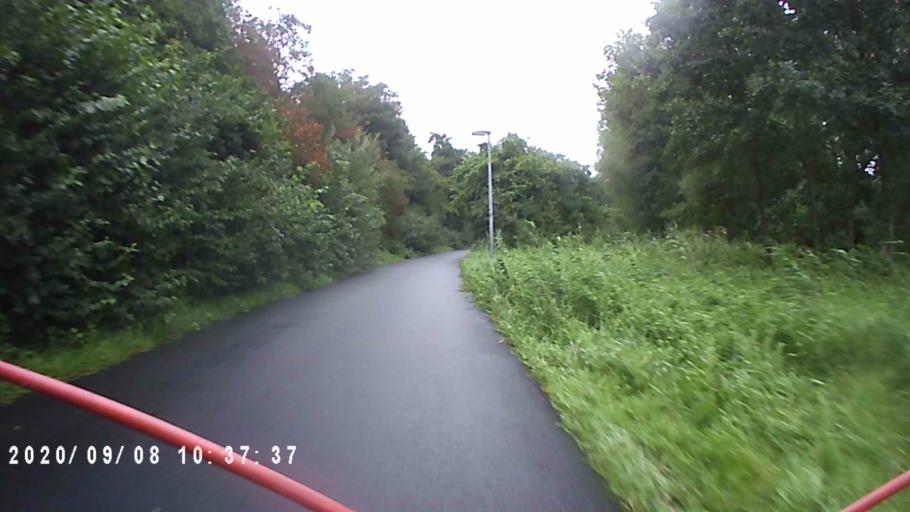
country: NL
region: Groningen
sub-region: Gemeente Groningen
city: Korrewegwijk
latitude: 53.2370
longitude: 6.5809
